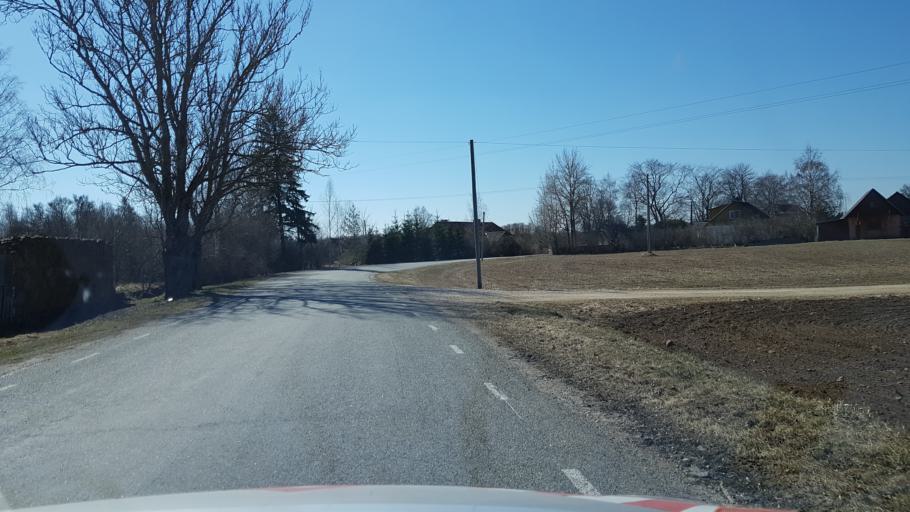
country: EE
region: Laeaene-Virumaa
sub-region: Rakke vald
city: Rakke
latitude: 59.0515
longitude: 26.4225
